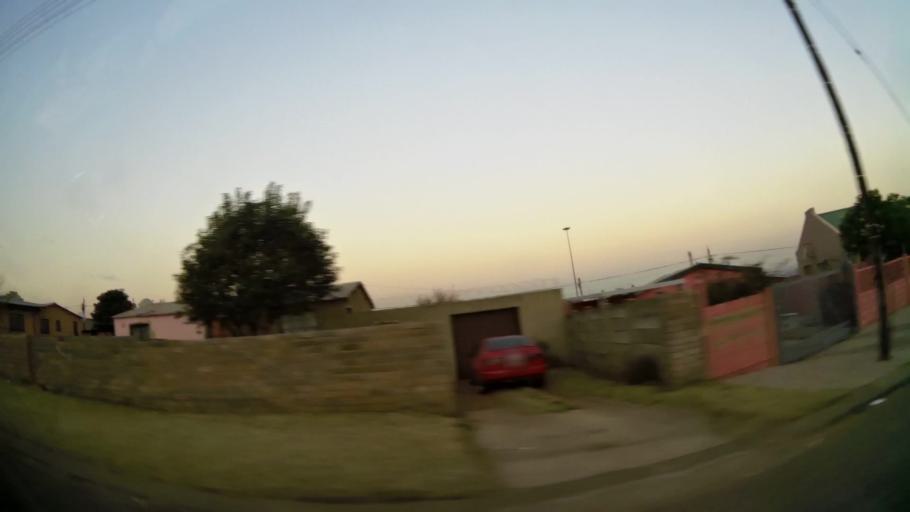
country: ZA
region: Gauteng
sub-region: West Rand District Municipality
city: Randfontein
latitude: -26.2074
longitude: 27.7148
